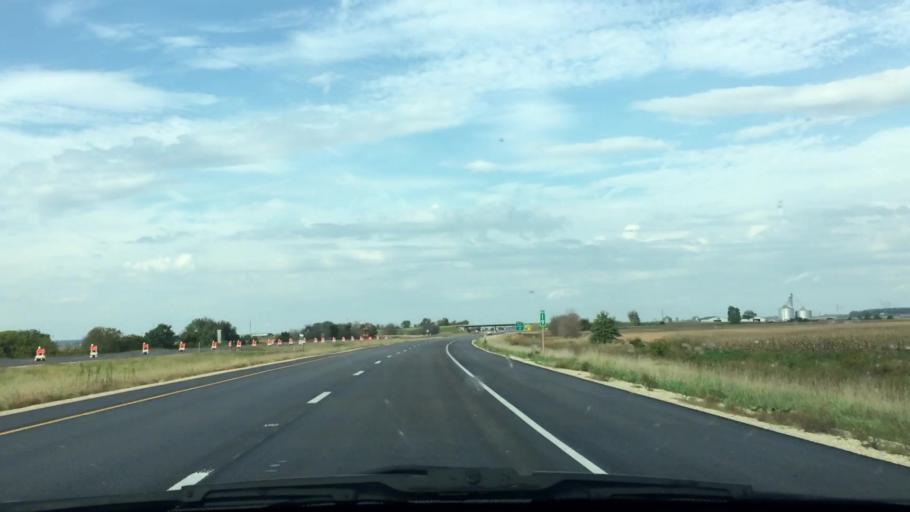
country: US
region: Illinois
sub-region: Whiteside County
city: Erie
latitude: 41.6894
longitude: -90.0866
